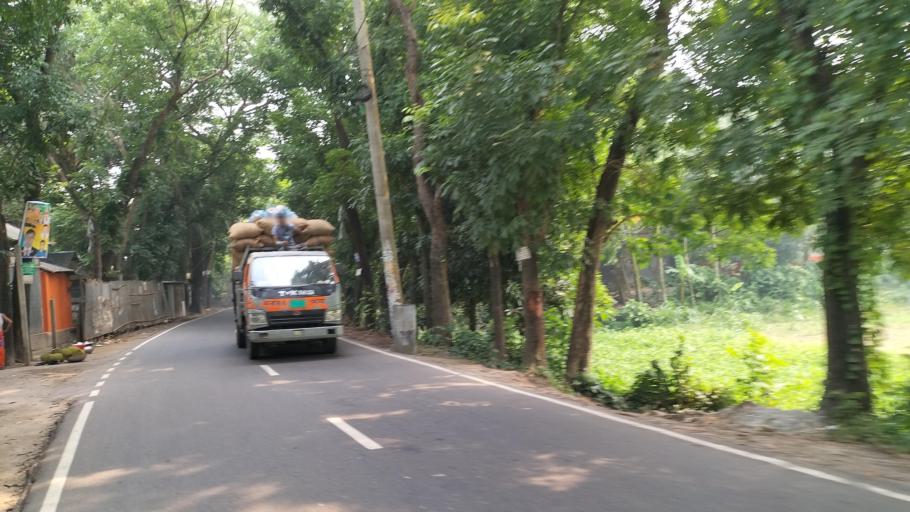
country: BD
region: Dhaka
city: Azimpur
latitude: 23.6993
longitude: 90.2943
